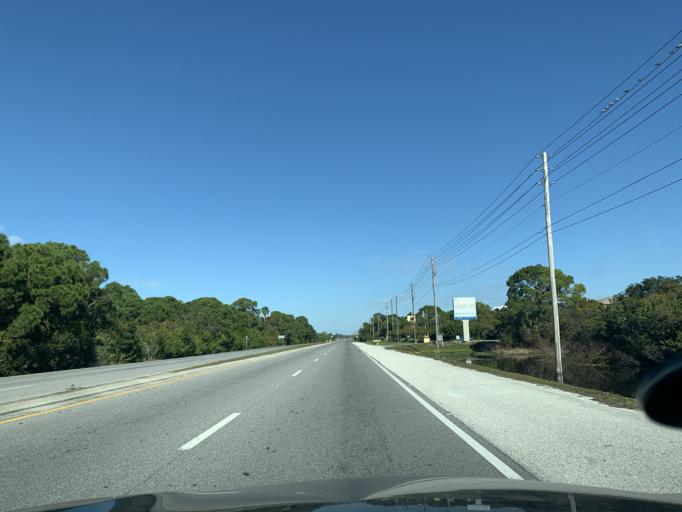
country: US
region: Florida
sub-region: Pinellas County
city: Bay Pines
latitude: 27.8226
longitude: -82.7538
